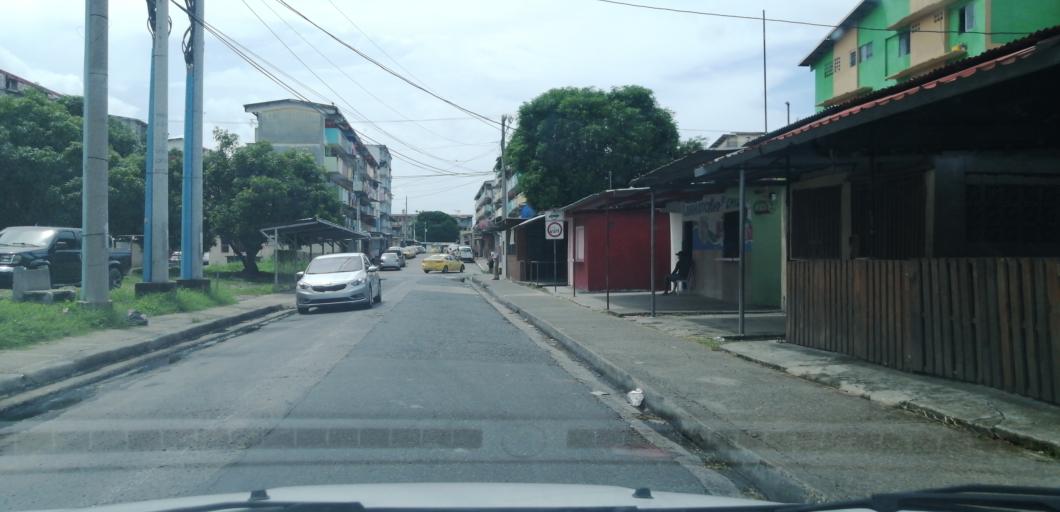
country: PA
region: Panama
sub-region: Distrito de Panama
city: Ancon
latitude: 8.9493
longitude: -79.5478
